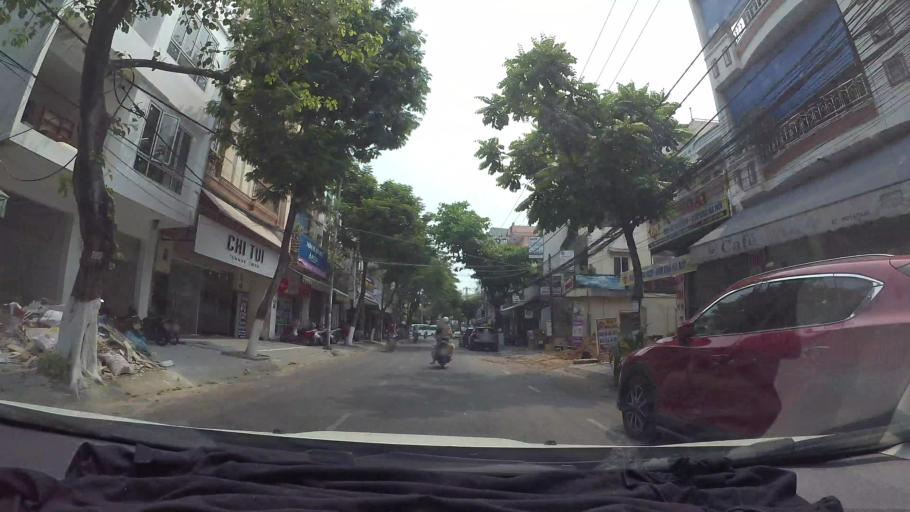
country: VN
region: Da Nang
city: Da Nang
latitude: 16.0549
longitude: 108.2189
